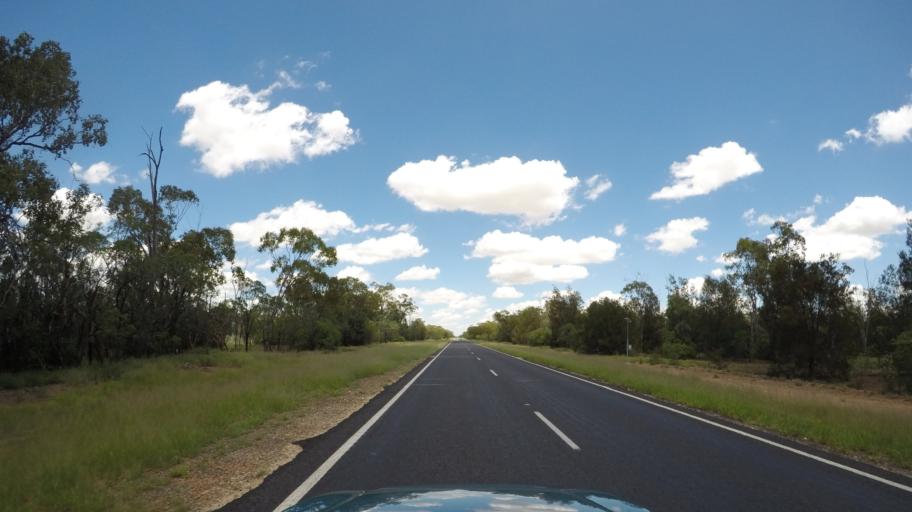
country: AU
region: Queensland
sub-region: Goondiwindi
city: Goondiwindi
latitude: -28.1662
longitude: 150.6030
